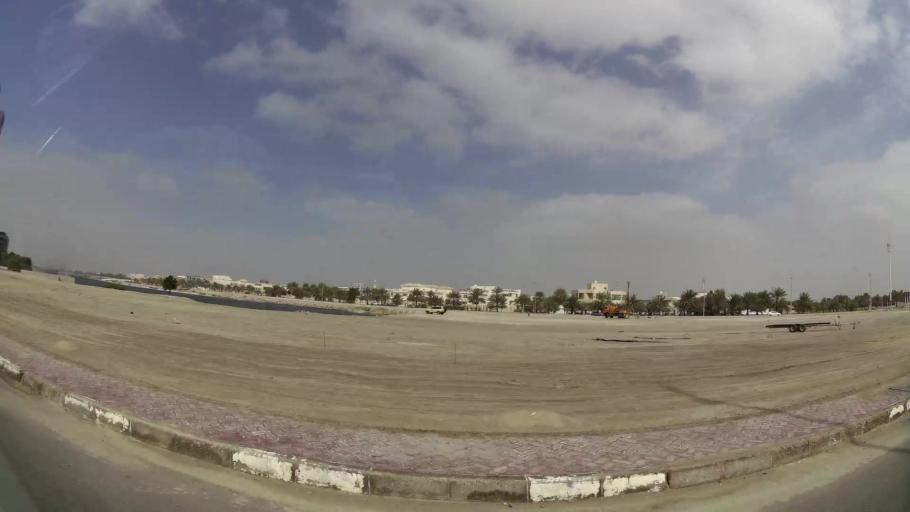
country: AE
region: Abu Dhabi
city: Abu Dhabi
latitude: 24.3956
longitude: 54.5208
